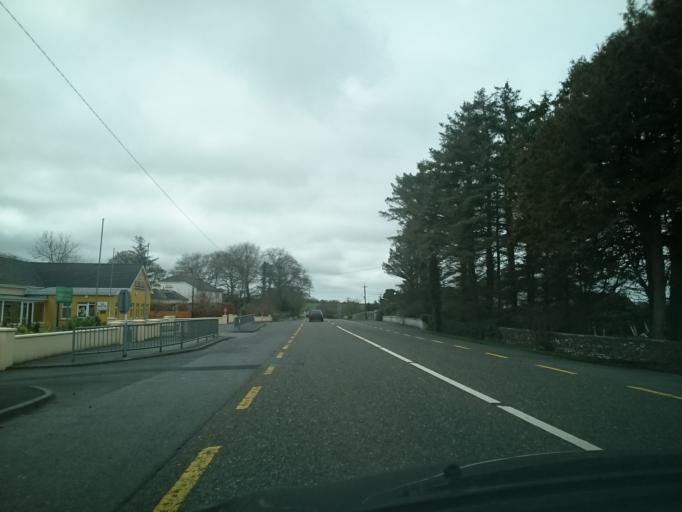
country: IE
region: Connaught
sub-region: Maigh Eo
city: Castlebar
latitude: 53.8189
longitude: -9.3860
